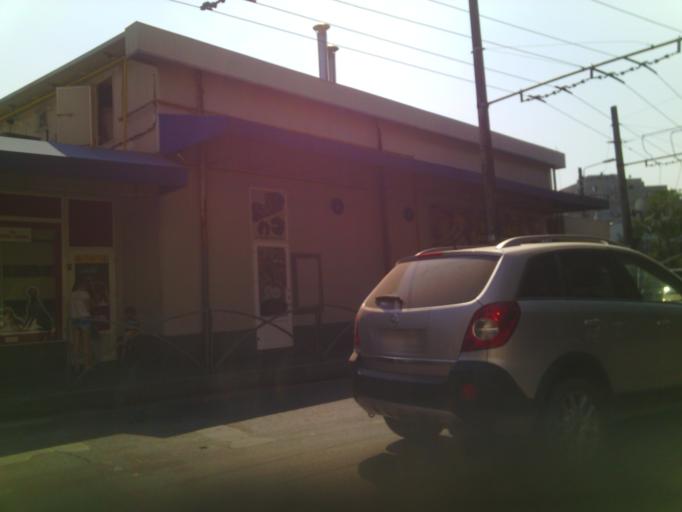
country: RO
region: Bucuresti
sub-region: Municipiul Bucuresti
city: Bucuresti
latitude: 44.3801
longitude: 26.0991
